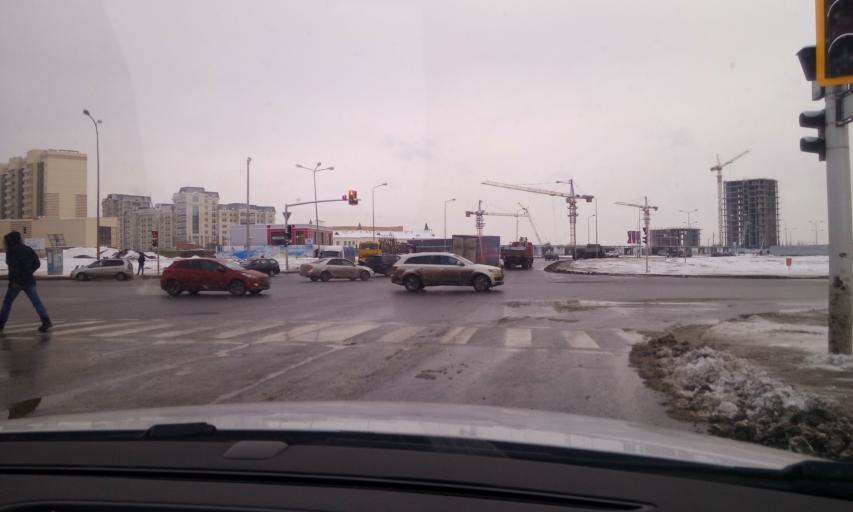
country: KZ
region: Astana Qalasy
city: Astana
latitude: 51.1263
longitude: 71.4864
